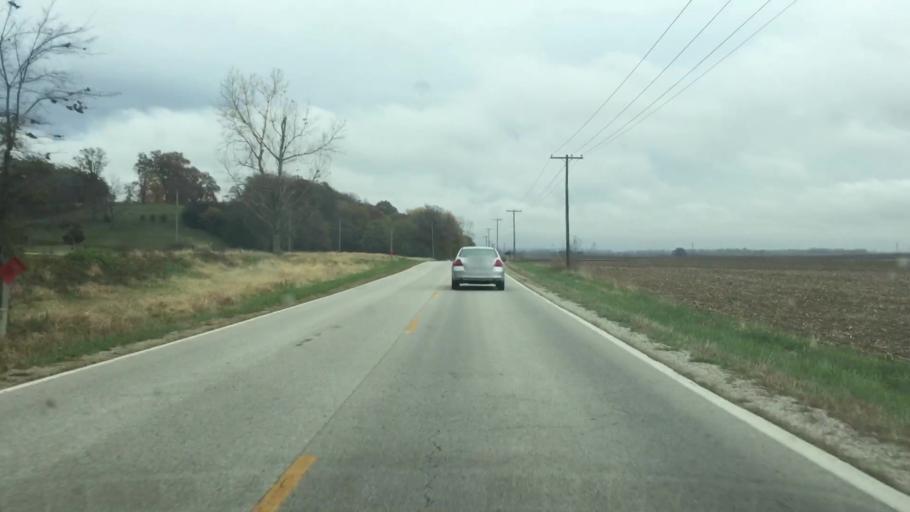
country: US
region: Missouri
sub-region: Gasconade County
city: Hermann
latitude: 38.7236
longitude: -91.4927
